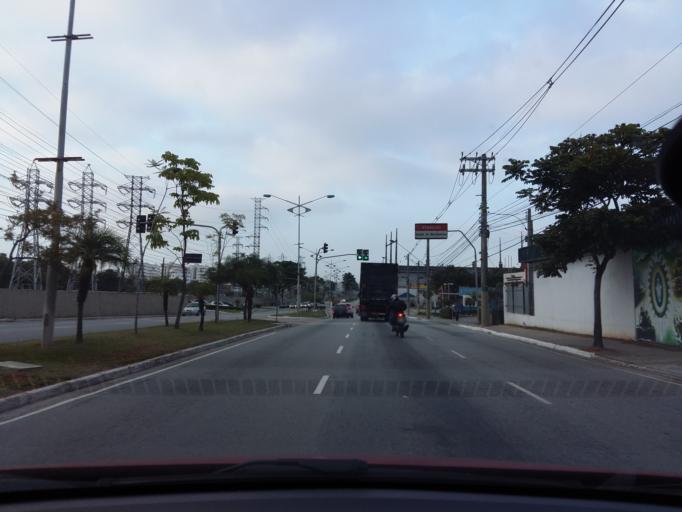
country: BR
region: Sao Paulo
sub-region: Sao Caetano Do Sul
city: Sao Caetano do Sul
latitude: -23.6231
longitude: -46.5819
